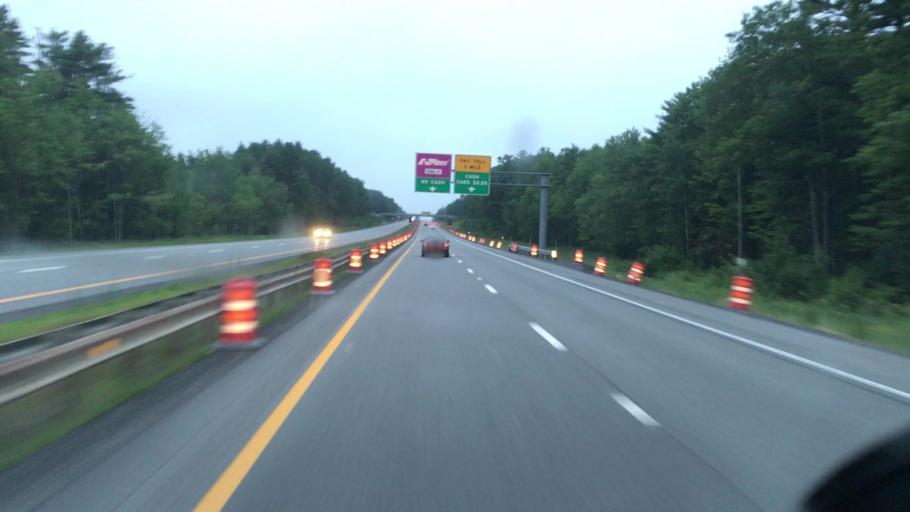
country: US
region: Maine
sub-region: Cumberland County
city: New Gloucester
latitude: 43.9176
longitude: -70.3382
